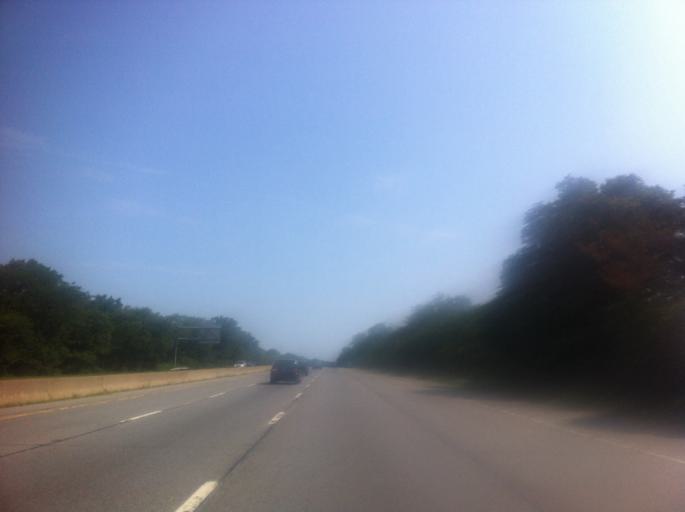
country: US
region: New York
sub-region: Nassau County
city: Plainview
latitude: 40.7948
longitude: -73.4889
